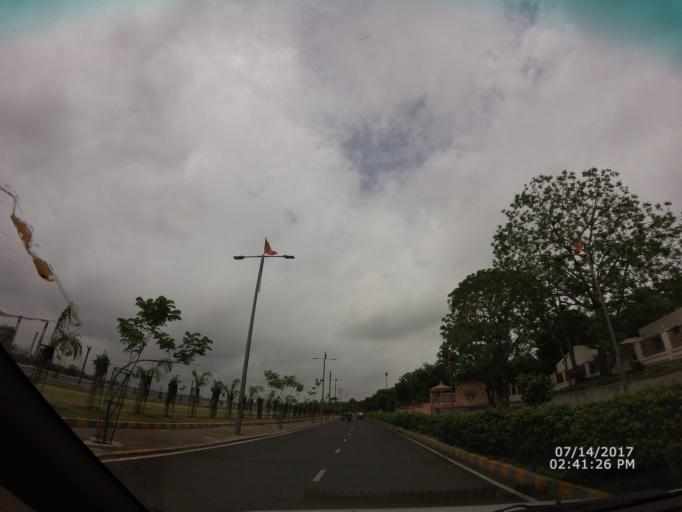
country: IN
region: Gujarat
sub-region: Ahmadabad
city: Ahmedabad
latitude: 23.0635
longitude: 72.5942
